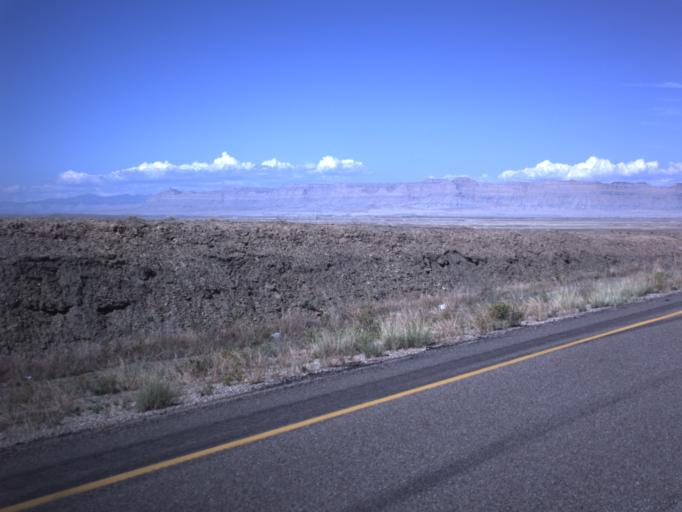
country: US
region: Utah
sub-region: Carbon County
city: East Carbon City
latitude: 38.9404
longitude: -110.3341
